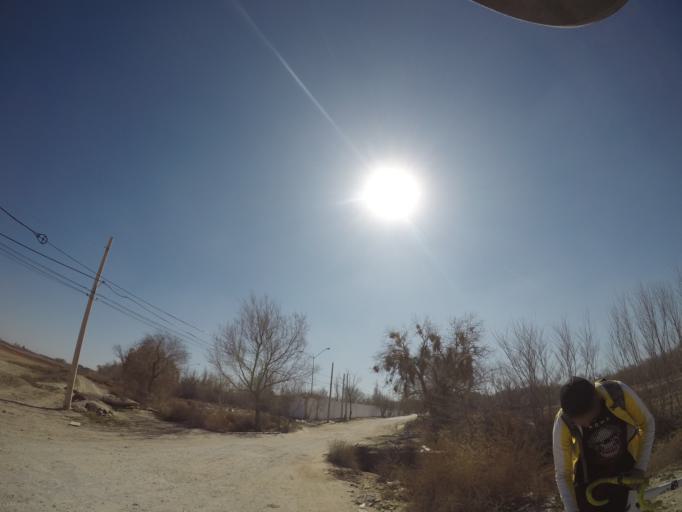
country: US
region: Texas
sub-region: El Paso County
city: Socorro
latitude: 31.6603
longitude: -106.3727
